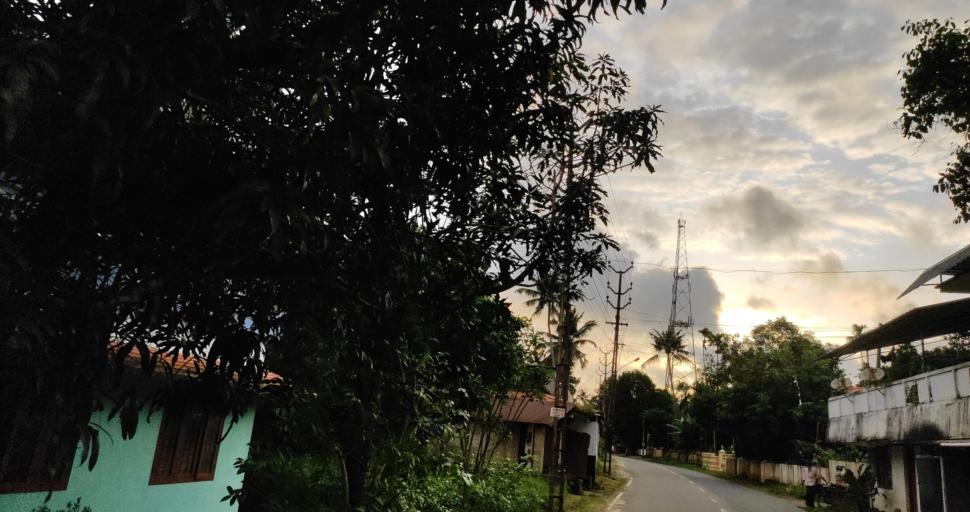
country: IN
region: Kerala
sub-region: Thrissur District
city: Kizhake Chalakudi
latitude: 10.3110
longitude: 76.3938
